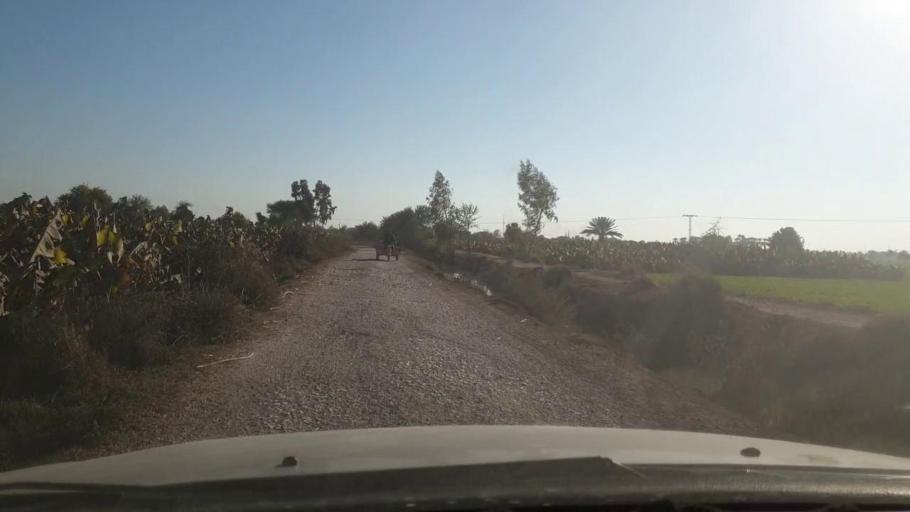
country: PK
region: Sindh
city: Adilpur
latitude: 27.9470
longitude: 69.2187
